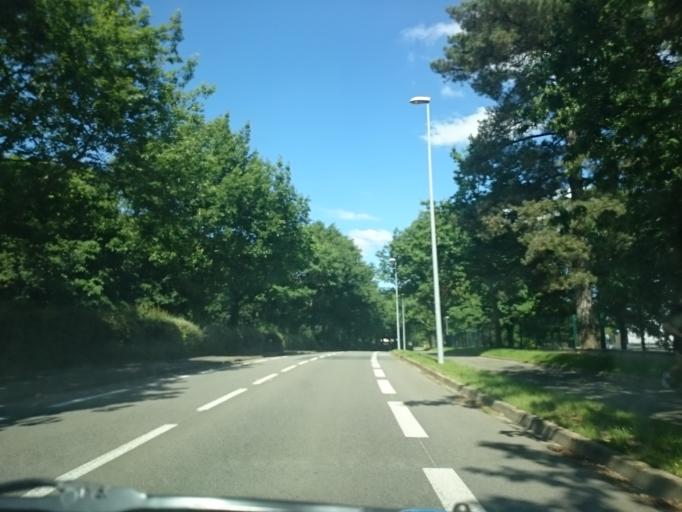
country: FR
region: Brittany
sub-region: Departement d'Ille-et-Vilaine
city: Cesson-Sevigne
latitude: 48.1227
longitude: -1.6265
